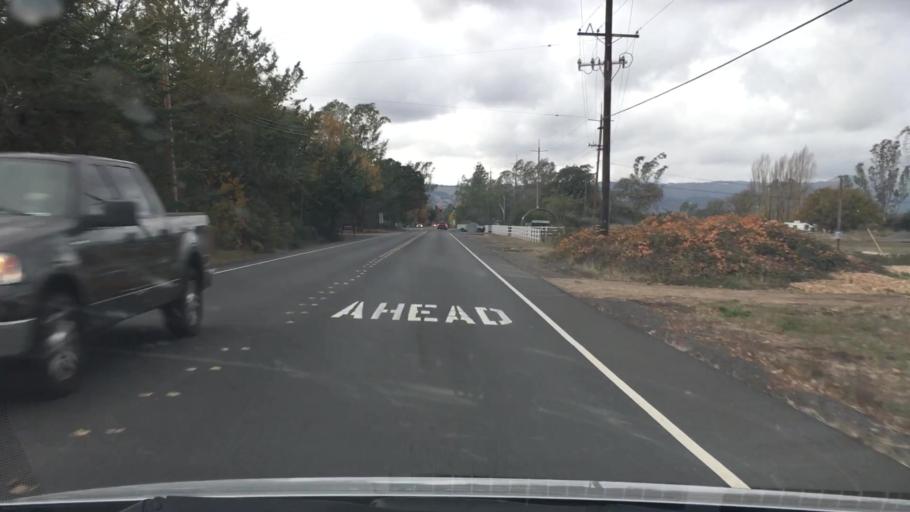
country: US
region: California
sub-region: Sonoma County
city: Sonoma
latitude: 38.2724
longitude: -122.4354
